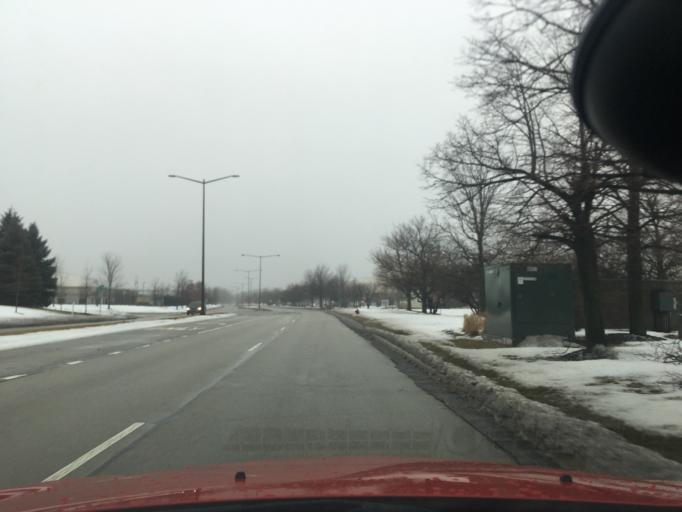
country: US
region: Illinois
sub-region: Kane County
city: North Aurora
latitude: 41.7952
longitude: -88.2616
